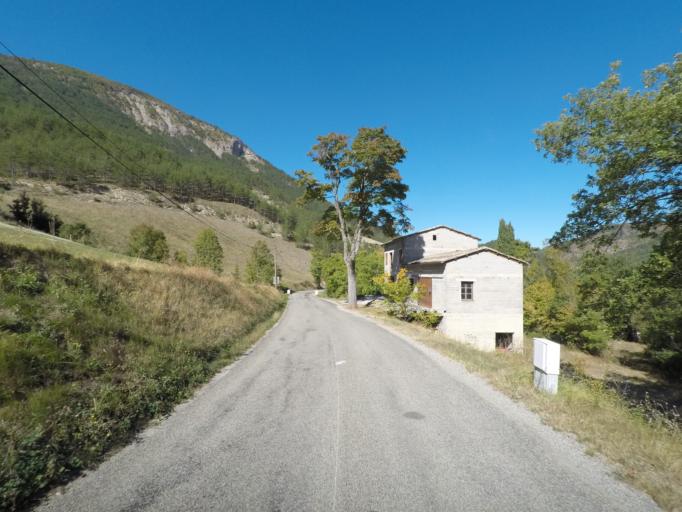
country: FR
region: Rhone-Alpes
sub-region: Departement de la Drome
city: Die
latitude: 44.6643
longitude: 5.2712
